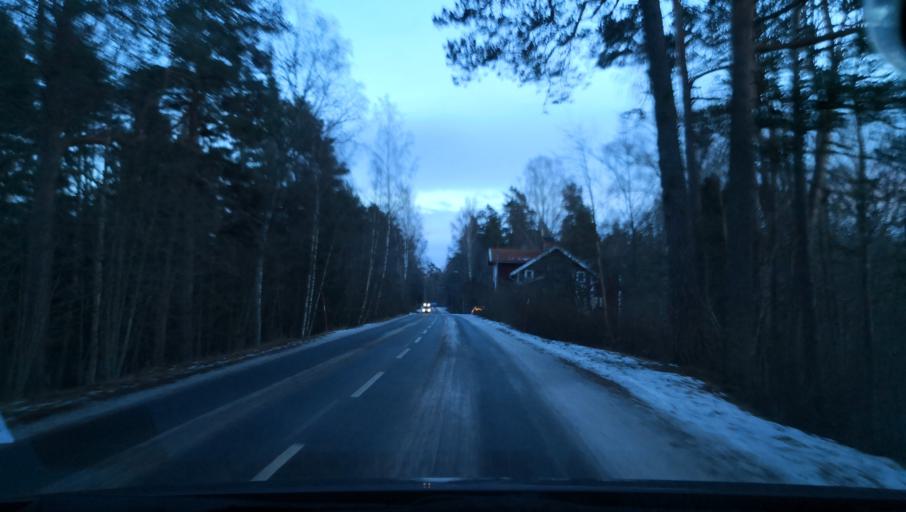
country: SE
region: Soedermanland
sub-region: Katrineholms Kommun
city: Katrineholm
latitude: 59.0853
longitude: 16.2183
